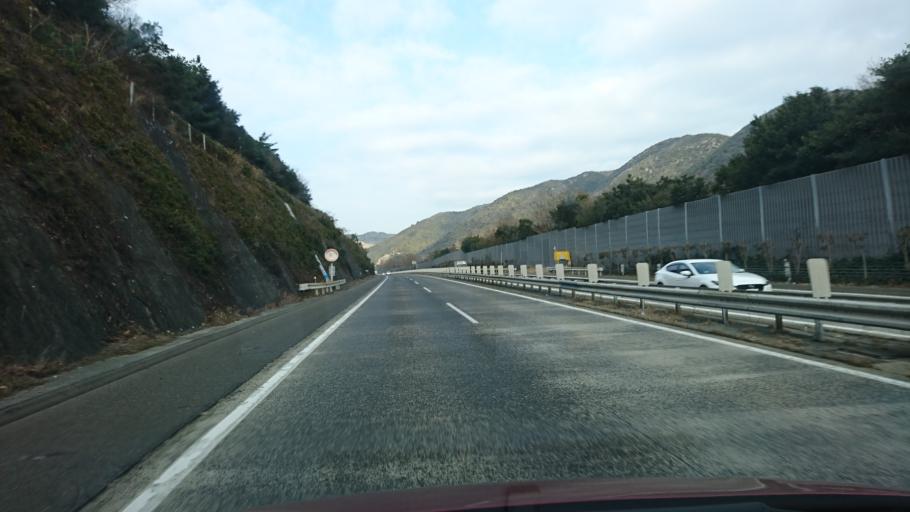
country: JP
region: Hyogo
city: Kariya
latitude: 34.7750
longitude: 134.3591
